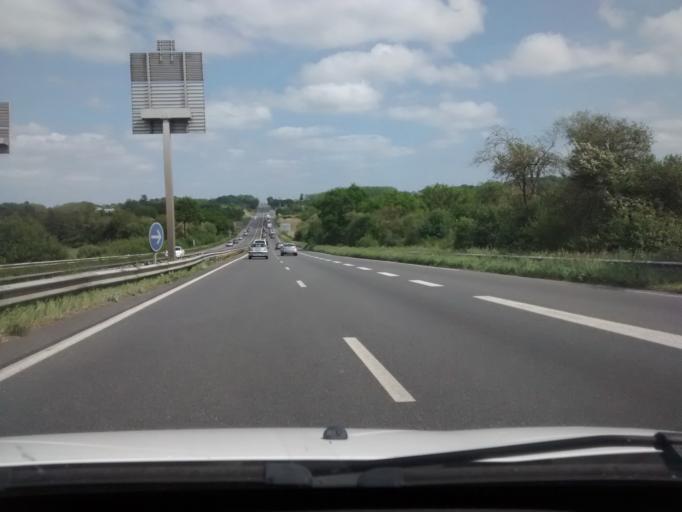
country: FR
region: Brittany
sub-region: Departement des Cotes-d'Armor
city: Lamballe
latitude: 48.4589
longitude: -2.5289
